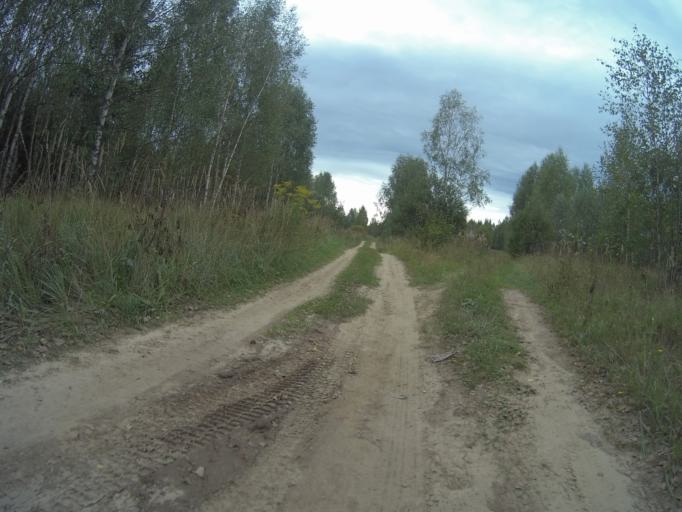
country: RU
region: Vladimir
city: Golovino
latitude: 55.9814
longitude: 40.5089
